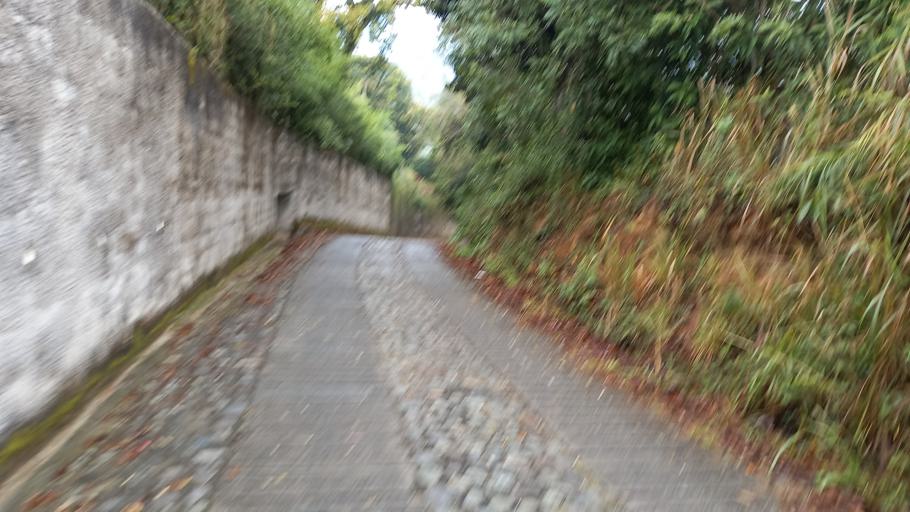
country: CO
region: Antioquia
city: Santa Barbara
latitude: 5.8481
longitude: -75.5751
